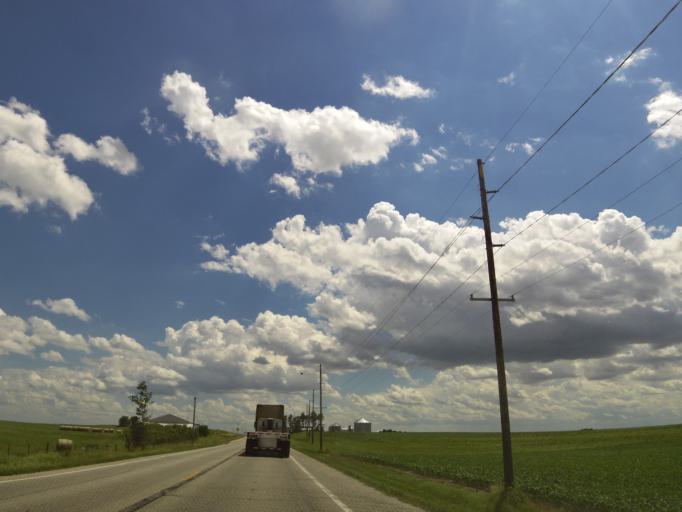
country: US
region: Iowa
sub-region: Benton County
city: Urbana
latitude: 42.2899
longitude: -91.8900
